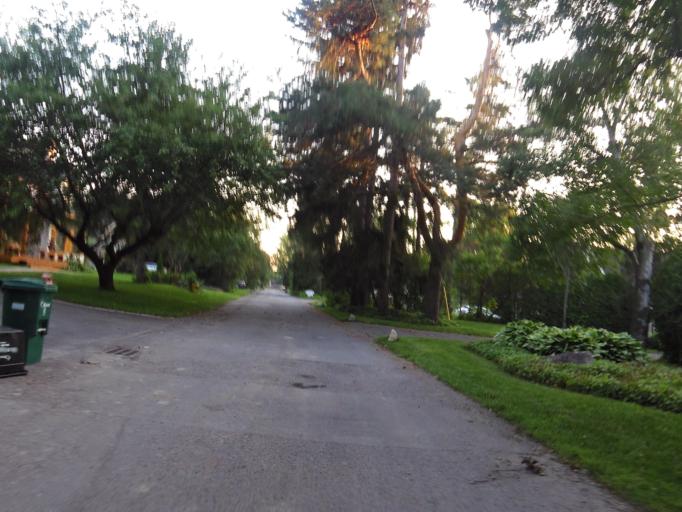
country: CA
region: Ontario
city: Bells Corners
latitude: 45.3538
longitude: -75.8363
